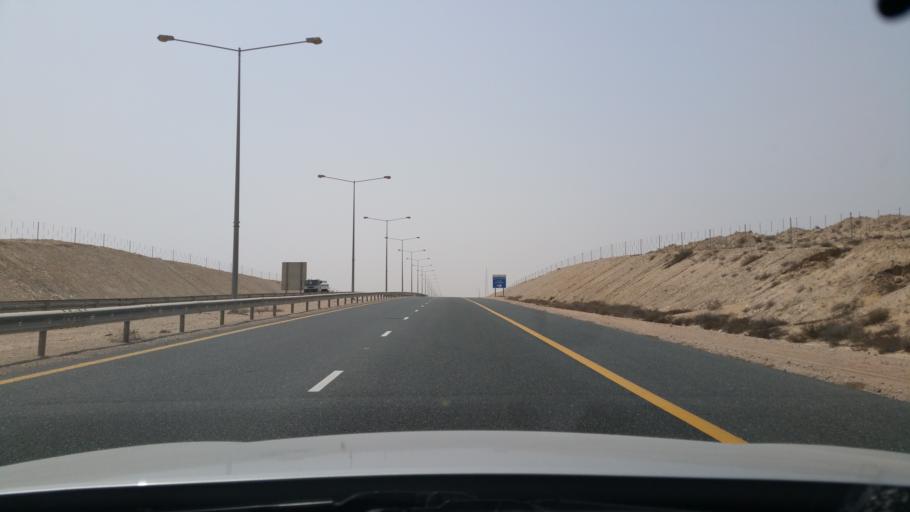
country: QA
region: Baladiyat ar Rayyan
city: Dukhan
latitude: 25.3292
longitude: 50.7857
